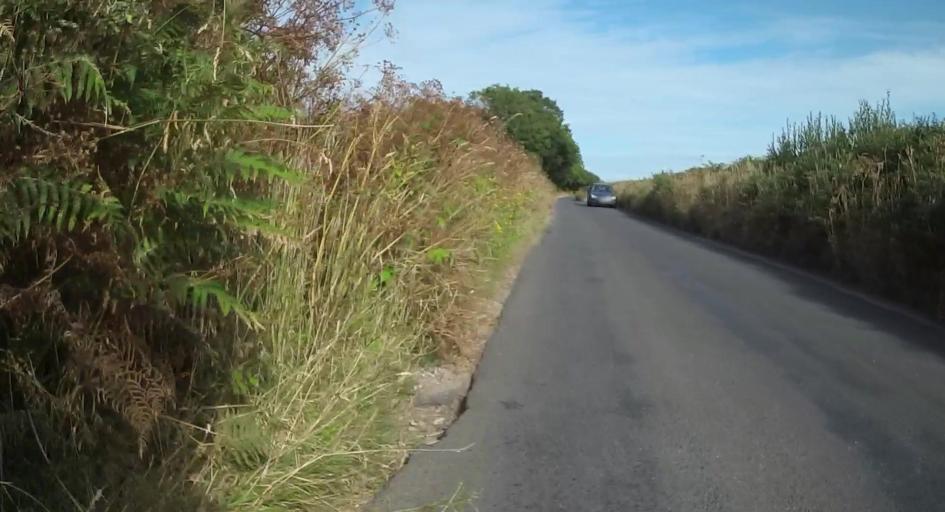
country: GB
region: England
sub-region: Dorset
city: Wareham
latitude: 50.6762
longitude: -2.1045
